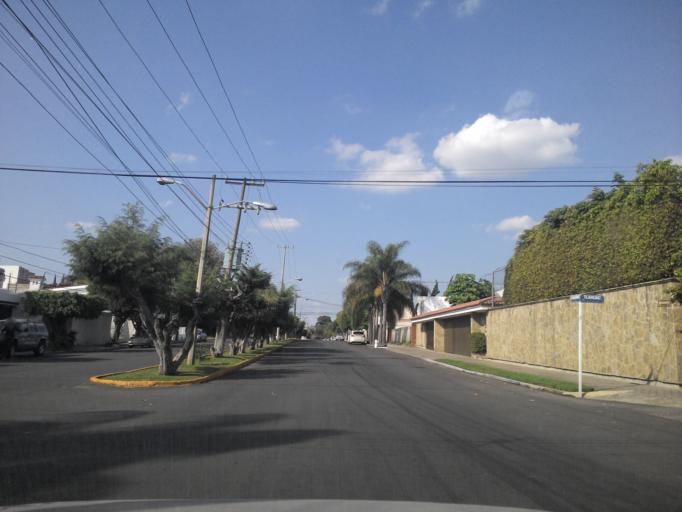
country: MX
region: Jalisco
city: Guadalajara
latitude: 20.6553
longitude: -103.4084
